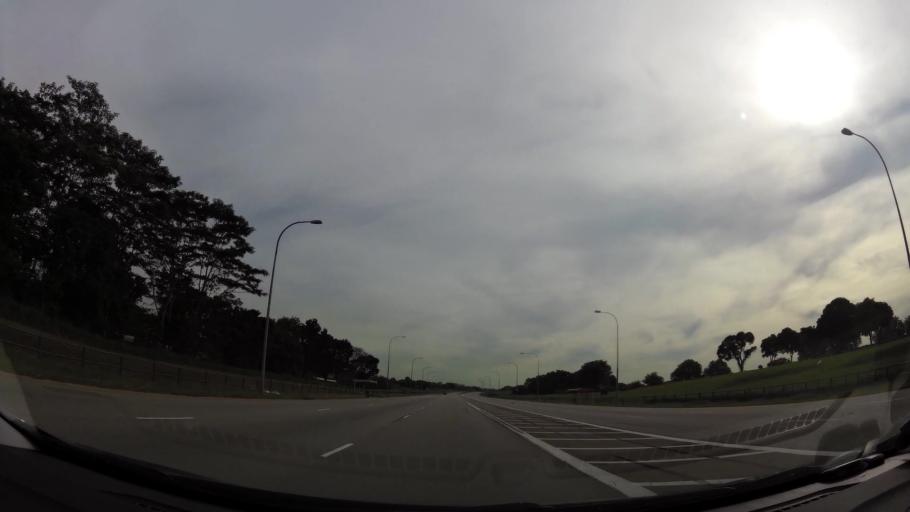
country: MY
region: Johor
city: Johor Bahru
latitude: 1.3807
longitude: 103.6968
